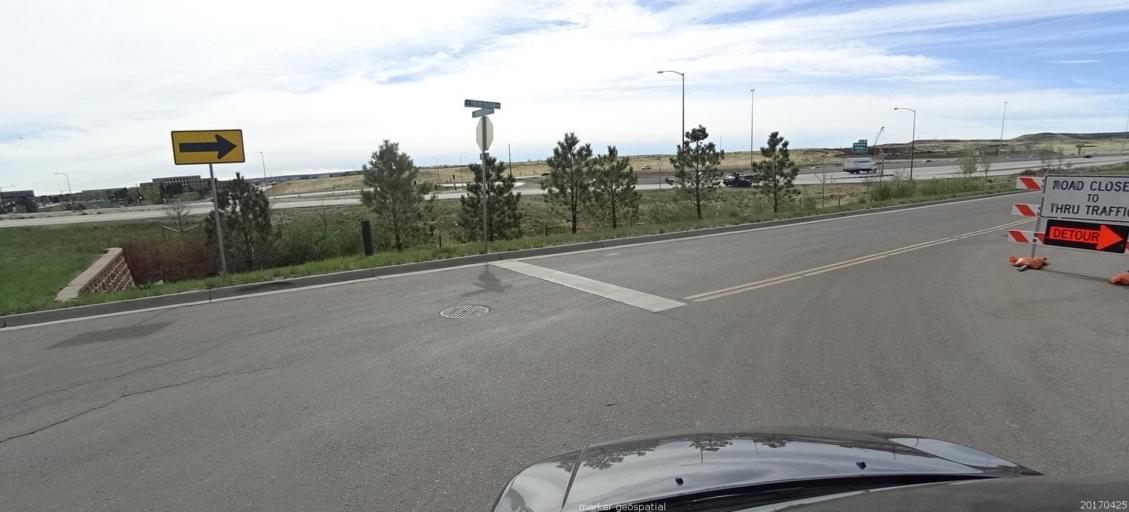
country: US
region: Colorado
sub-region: Douglas County
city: Meridian
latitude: 39.5352
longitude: -104.8696
